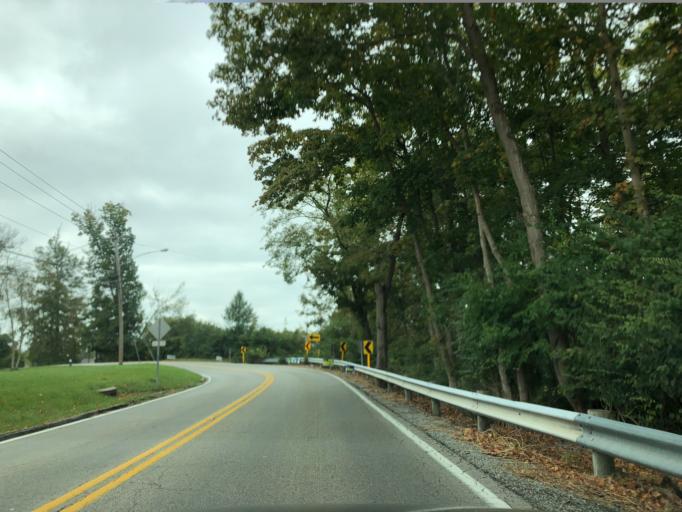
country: US
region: Ohio
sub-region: Hamilton County
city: Sixteen Mile Stand
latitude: 39.2678
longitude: -84.3077
